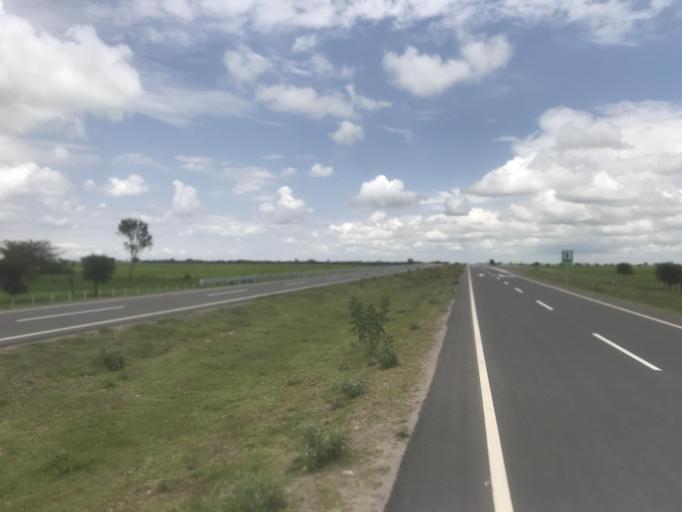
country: ET
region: Oromiya
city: Ziway
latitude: 8.2278
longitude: 38.8701
